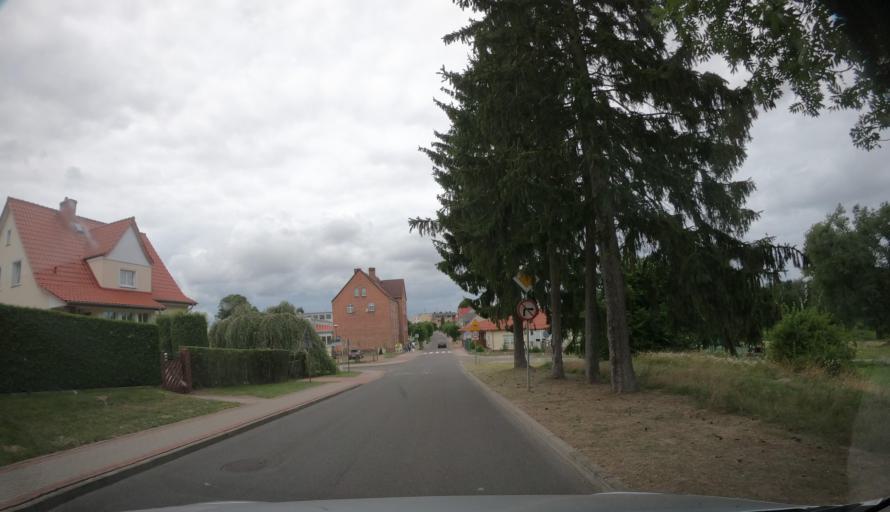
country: PL
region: West Pomeranian Voivodeship
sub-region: Powiat kamienski
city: Golczewo
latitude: 53.8210
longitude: 14.9800
